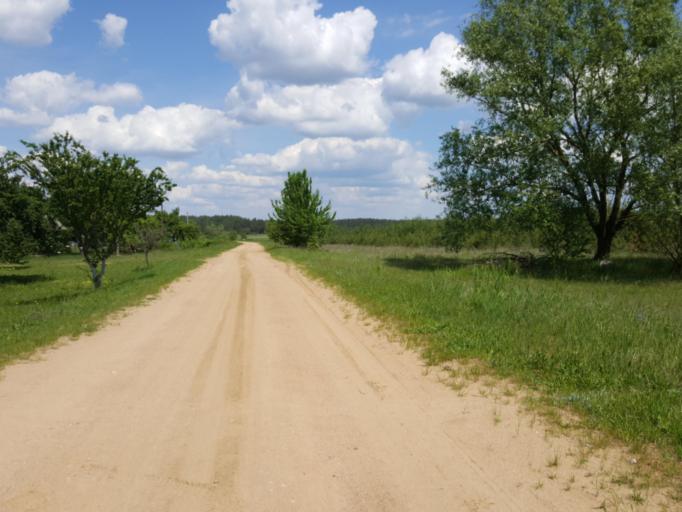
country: BY
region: Brest
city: Kamyanyuki
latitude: 52.5342
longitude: 23.6990
